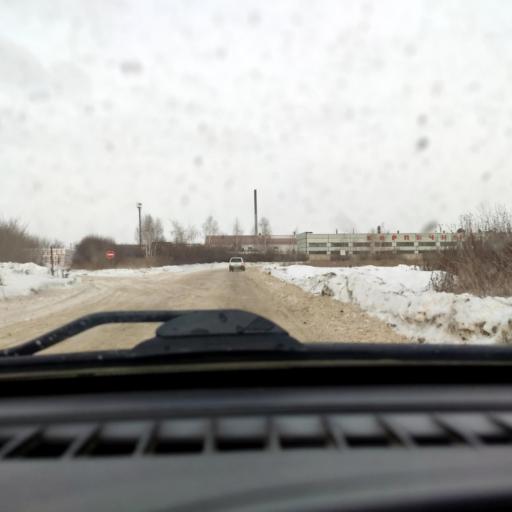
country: RU
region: Samara
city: Tol'yatti
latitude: 53.5829
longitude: 49.2603
